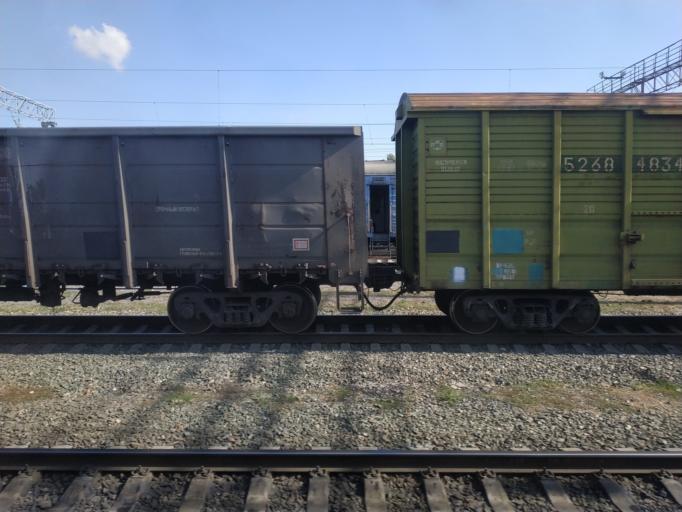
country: RU
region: Volgograd
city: Gumrak
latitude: 48.7790
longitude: 44.3784
